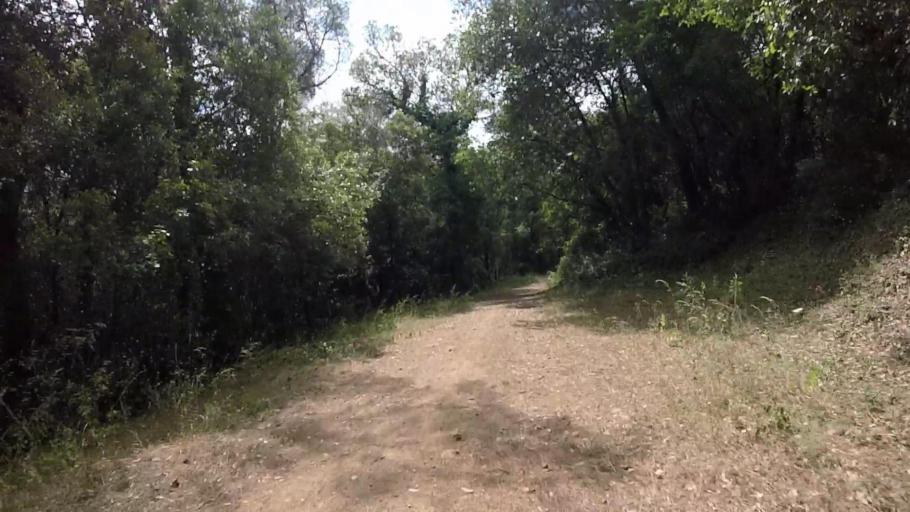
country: FR
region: Provence-Alpes-Cote d'Azur
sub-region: Departement des Alpes-Maritimes
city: Biot
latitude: 43.6163
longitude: 7.0903
